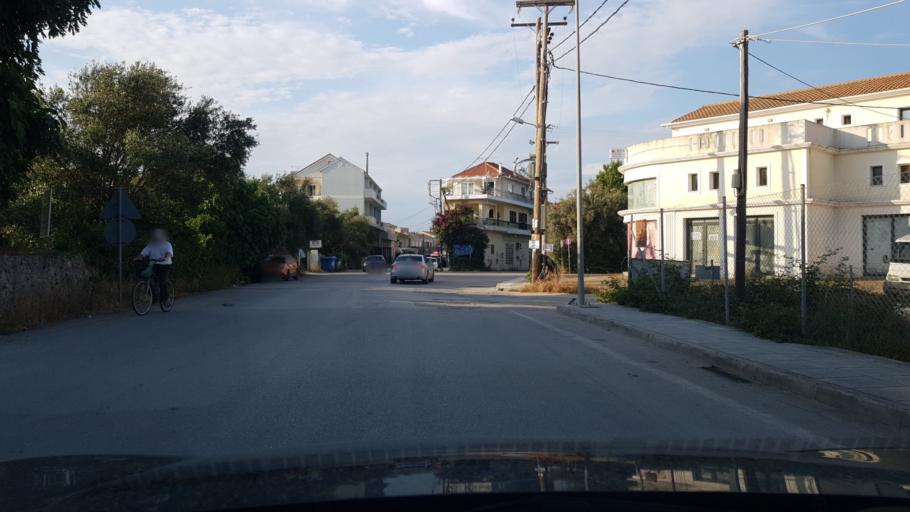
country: GR
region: Ionian Islands
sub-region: Lefkada
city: Lefkada
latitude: 38.8284
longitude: 20.7035
